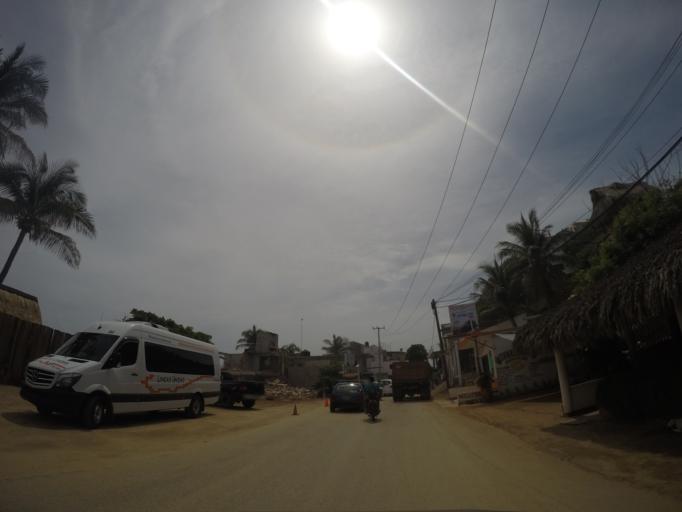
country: MX
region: Oaxaca
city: Santa Maria Tonameca
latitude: 15.6627
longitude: -96.5131
